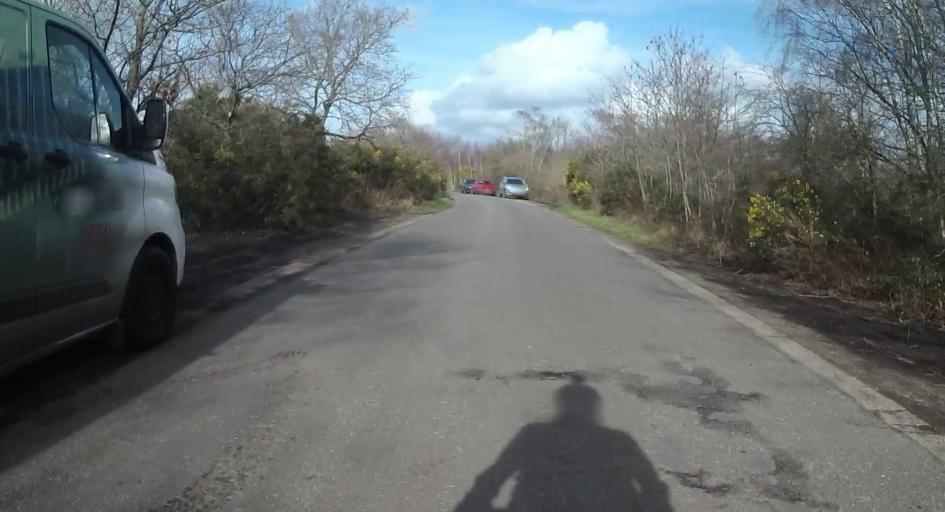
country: GB
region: England
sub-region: West Berkshire
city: Thatcham
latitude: 51.3773
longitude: -1.2534
